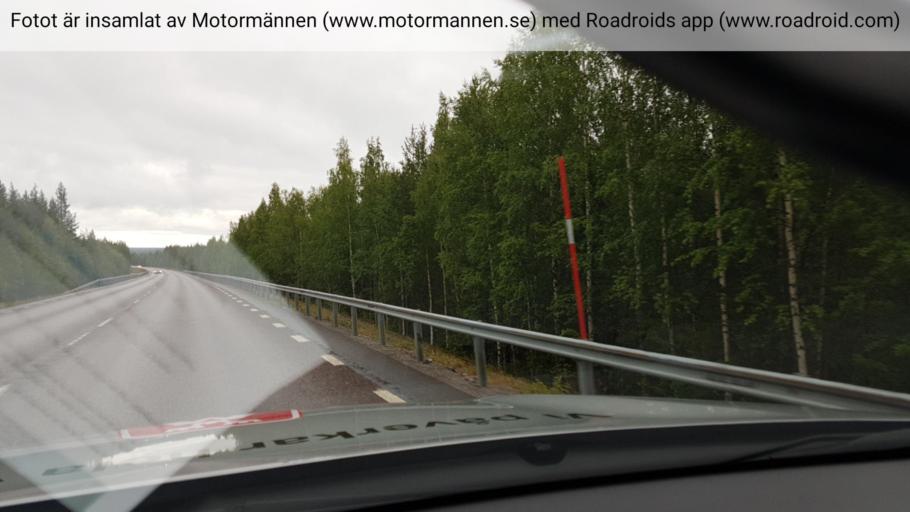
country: SE
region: Norrbotten
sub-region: Gallivare Kommun
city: Gaellivare
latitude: 67.1166
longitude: 20.7745
